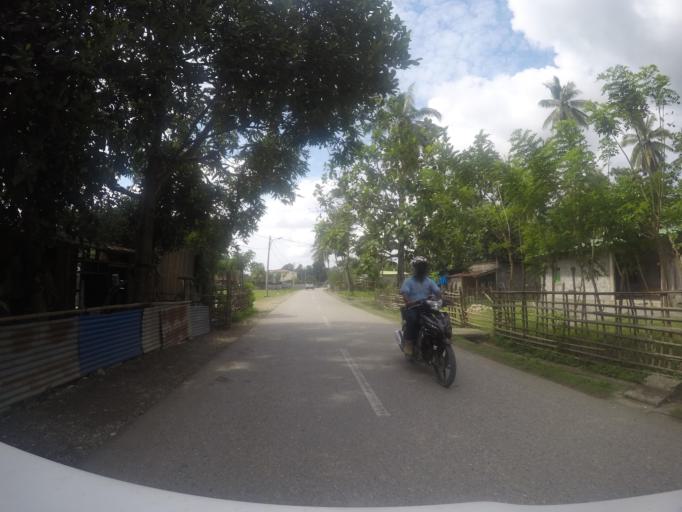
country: TL
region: Viqueque
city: Viqueque
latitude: -8.8531
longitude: 126.3641
